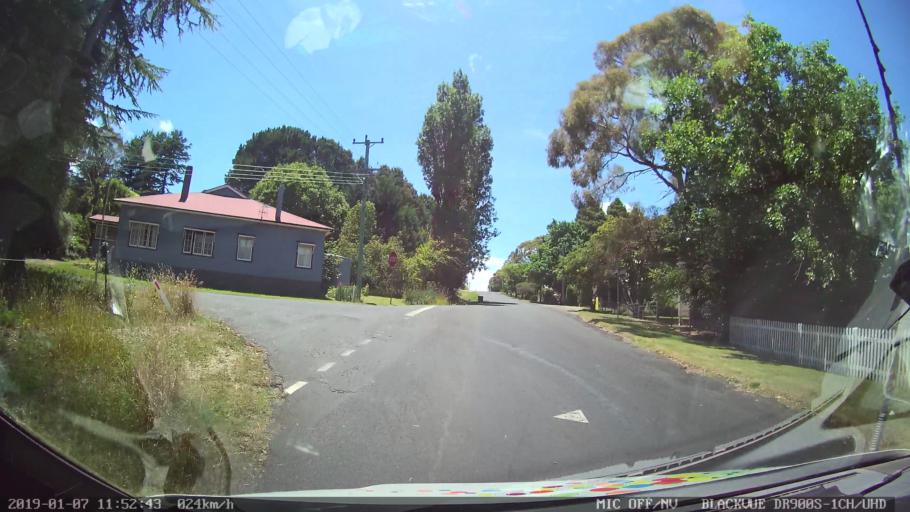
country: AU
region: New South Wales
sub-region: Guyra
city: Guyra
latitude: -30.3088
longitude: 151.6565
